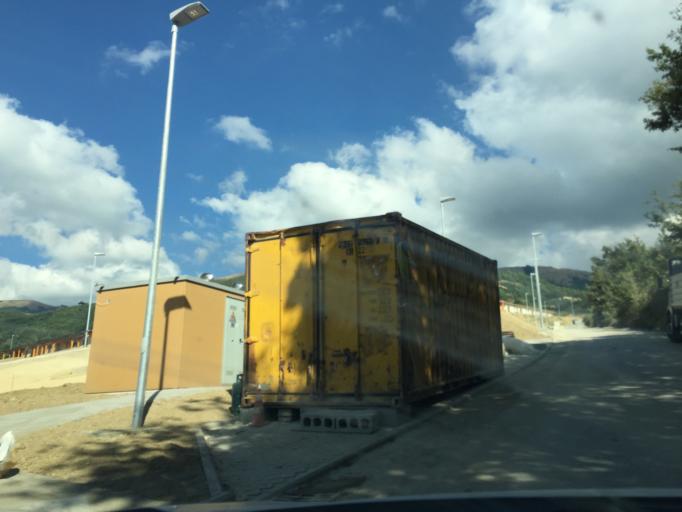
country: IT
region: Latium
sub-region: Provincia di Rieti
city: Accumoli
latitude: 42.6971
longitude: 13.2425
